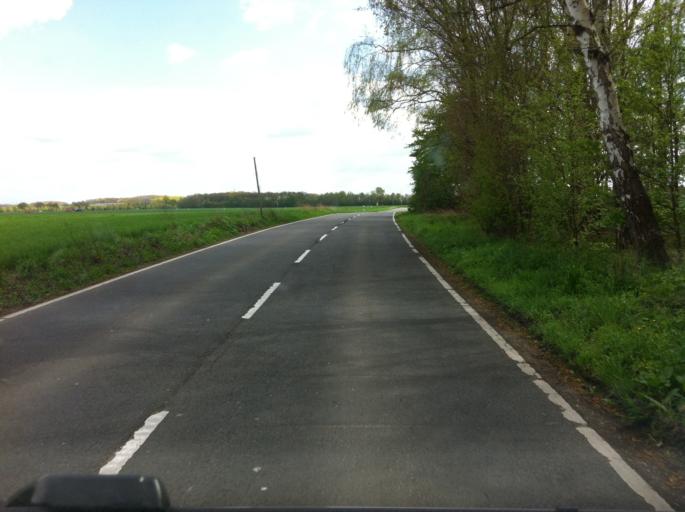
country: DE
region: North Rhine-Westphalia
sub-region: Regierungsbezirk Koln
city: Sinnersdorf
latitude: 51.0414
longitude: 6.8653
